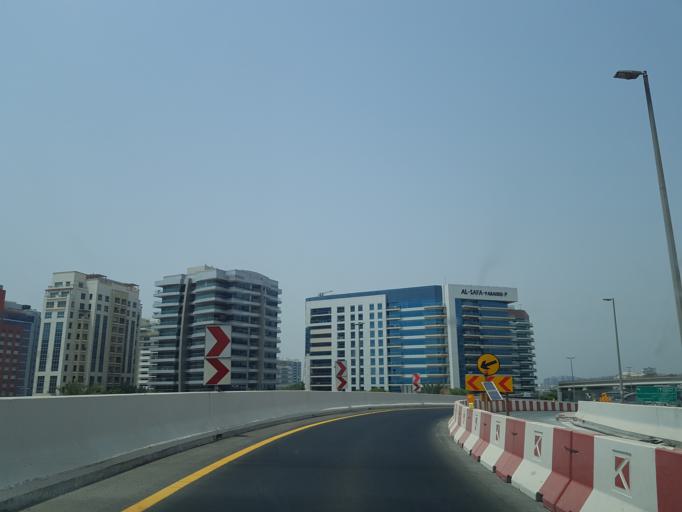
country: AE
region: Ash Shariqah
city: Sharjah
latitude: 25.2306
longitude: 55.3166
